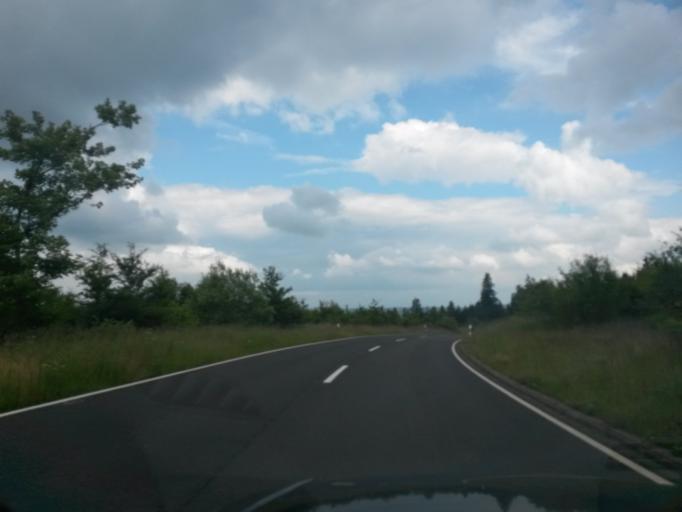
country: DE
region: Hesse
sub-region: Regierungsbezirk Kassel
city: Gersfeld
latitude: 50.5006
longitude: 9.9494
